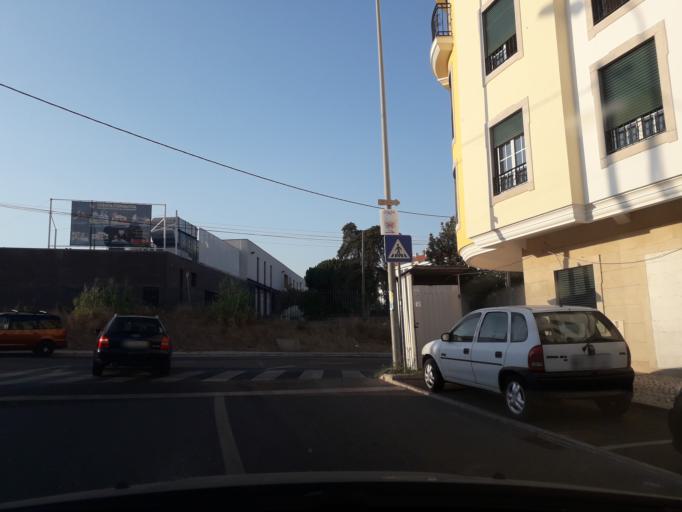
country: PT
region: Lisbon
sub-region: Amadora
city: Amadora
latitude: 38.7442
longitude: -9.2268
